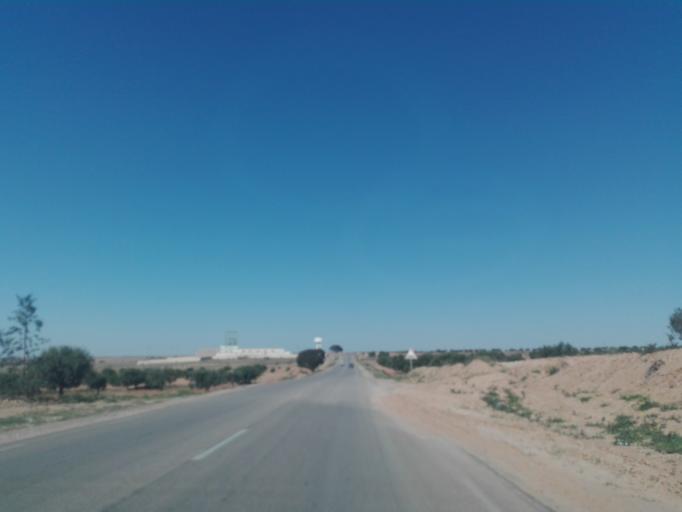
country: TN
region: Safaqis
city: Bi'r `Ali Bin Khalifah
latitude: 34.7393
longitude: 10.3999
